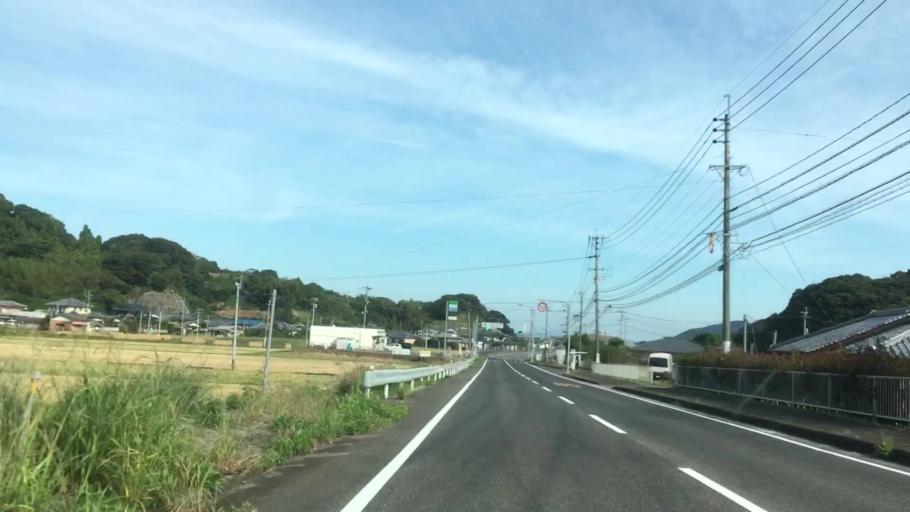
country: JP
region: Nagasaki
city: Sasebo
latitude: 32.9853
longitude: 129.6459
